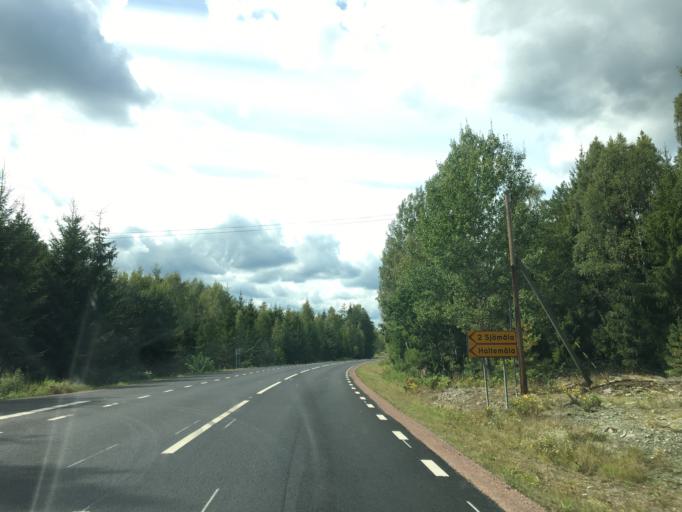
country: SE
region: Kalmar
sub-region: Nybro Kommun
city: Nybro
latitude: 56.9138
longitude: 16.0140
